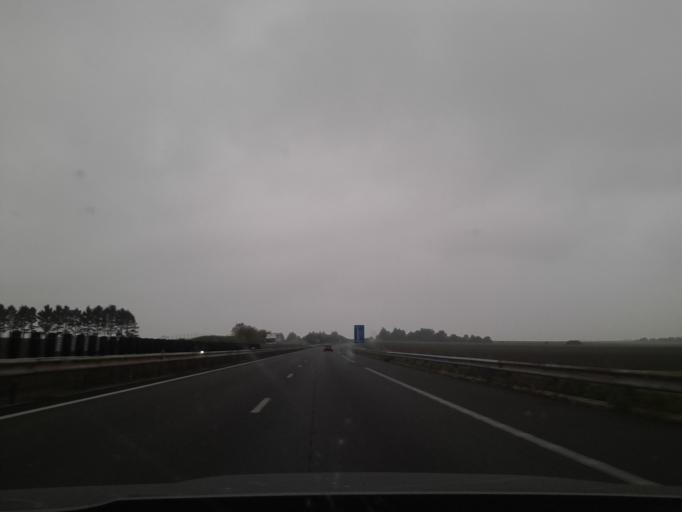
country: FR
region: Nord-Pas-de-Calais
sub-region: Departement du Nord
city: Fontaine-Notre-Dame
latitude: 50.1620
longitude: 3.1691
